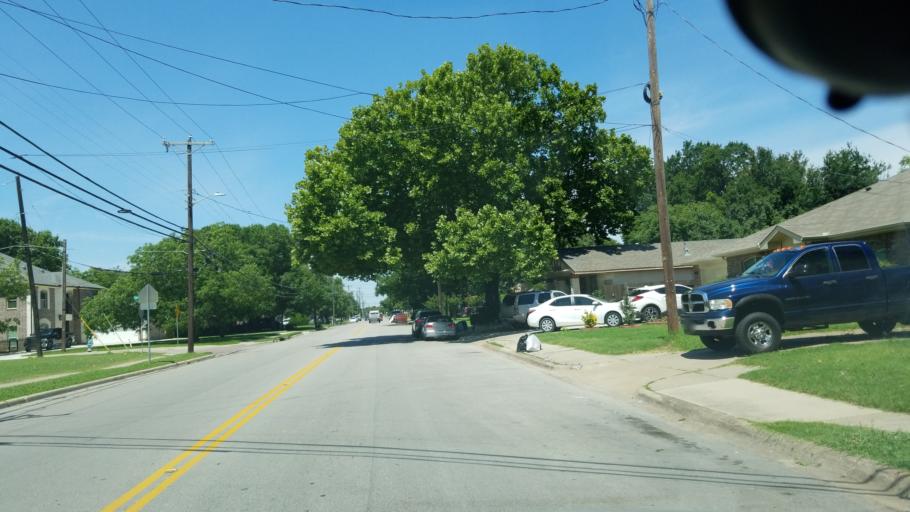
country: US
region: Texas
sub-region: Dallas County
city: Irving
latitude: 32.8176
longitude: -96.9301
